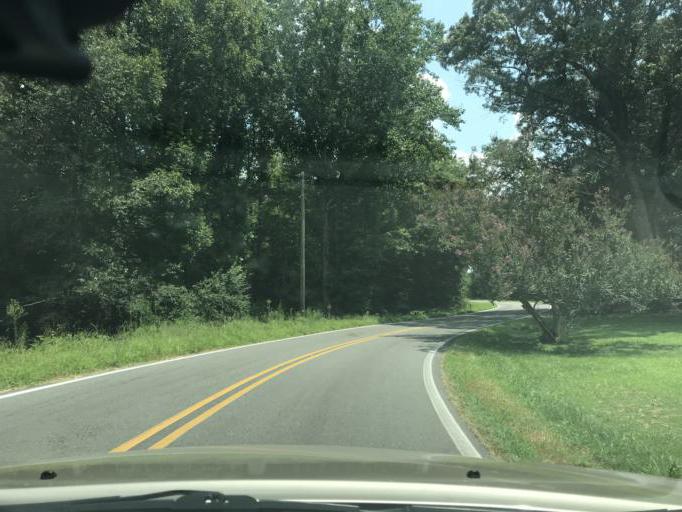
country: US
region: Georgia
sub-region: Forsyth County
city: Cumming
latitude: 34.2637
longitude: -84.2234
